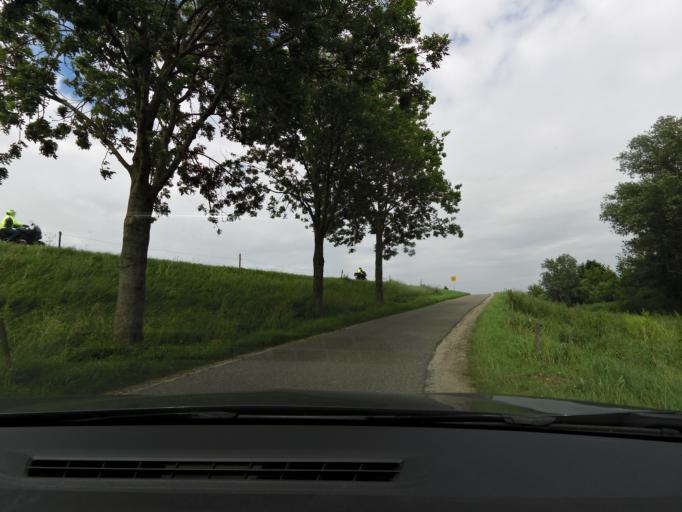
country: NL
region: South Holland
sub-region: Gemeente Brielle
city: Brielle
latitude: 51.9203
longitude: 4.1249
